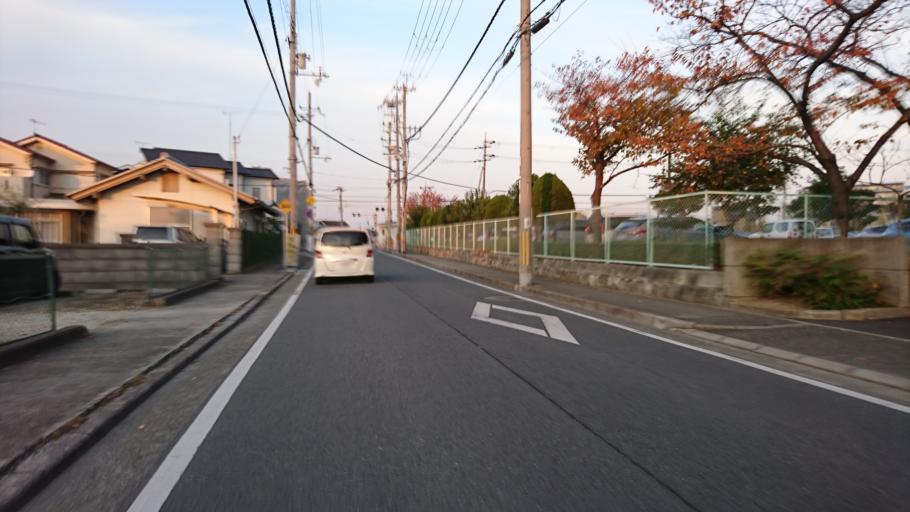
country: JP
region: Hyogo
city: Kakogawacho-honmachi
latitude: 34.7517
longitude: 134.8610
